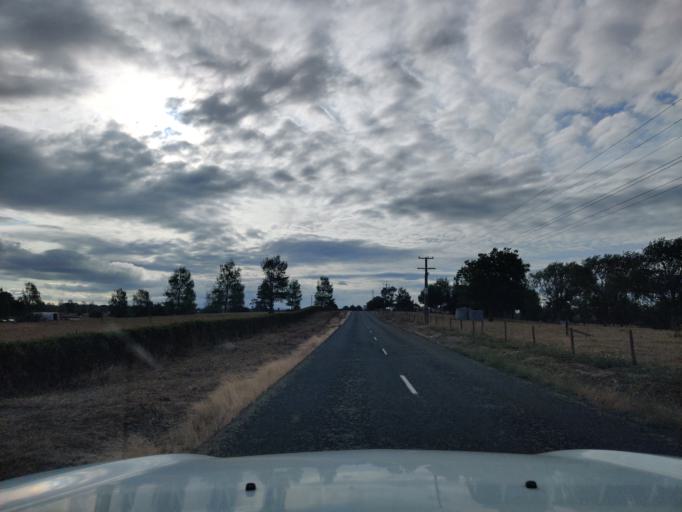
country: NZ
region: Waikato
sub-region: Waipa District
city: Cambridge
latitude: -37.7957
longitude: 175.4377
